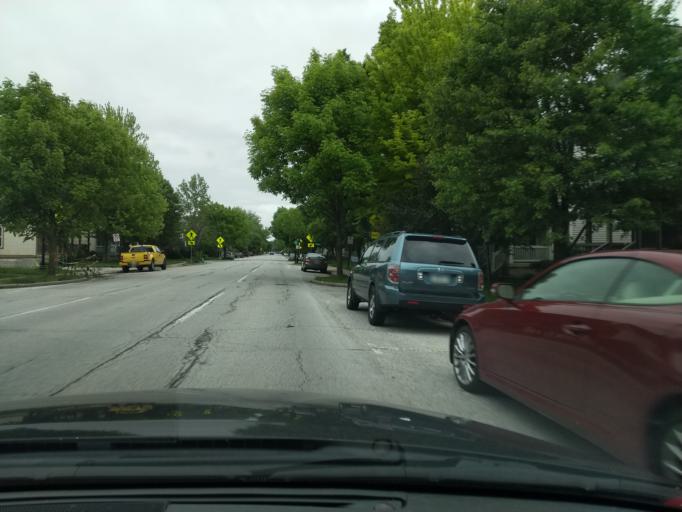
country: US
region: Indiana
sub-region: Marion County
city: Indianapolis
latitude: 39.7986
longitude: -86.1533
